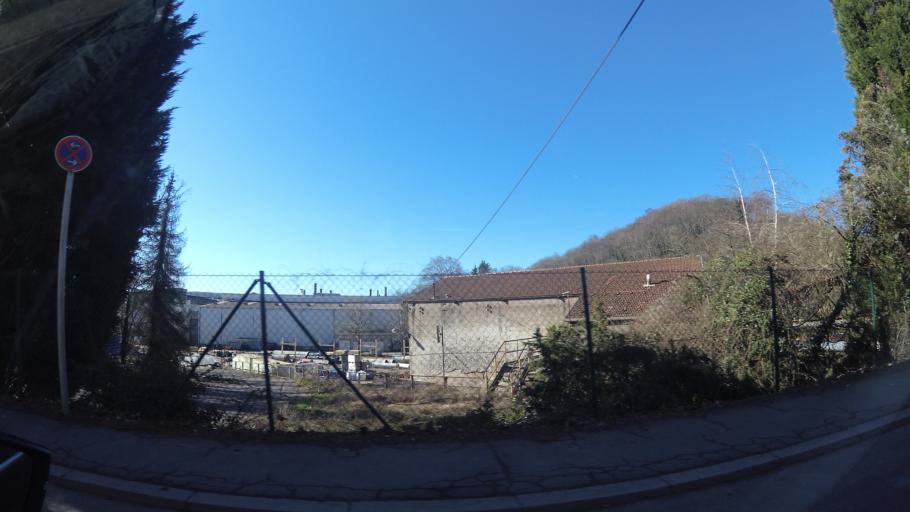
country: FR
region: Lorraine
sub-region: Departement de la Moselle
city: Alsting
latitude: 49.2169
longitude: 7.0414
